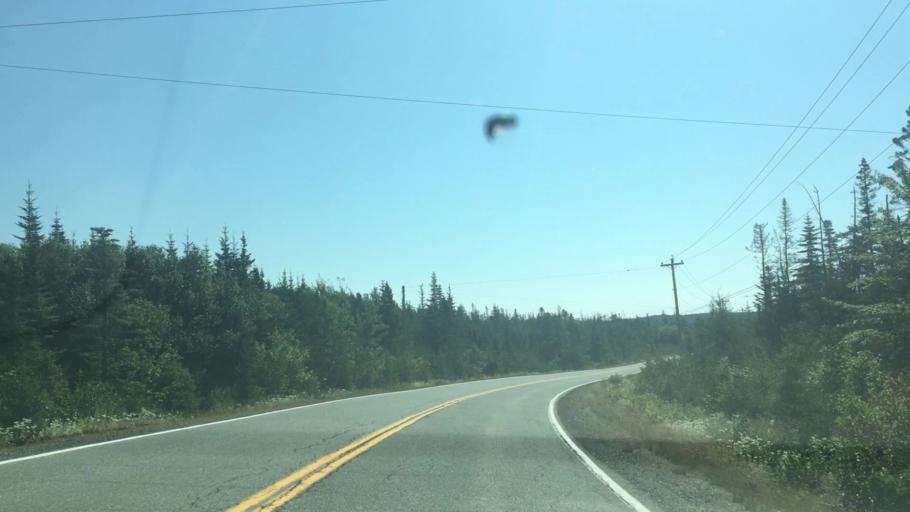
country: CA
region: Nova Scotia
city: Antigonish
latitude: 45.0109
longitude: -62.0913
